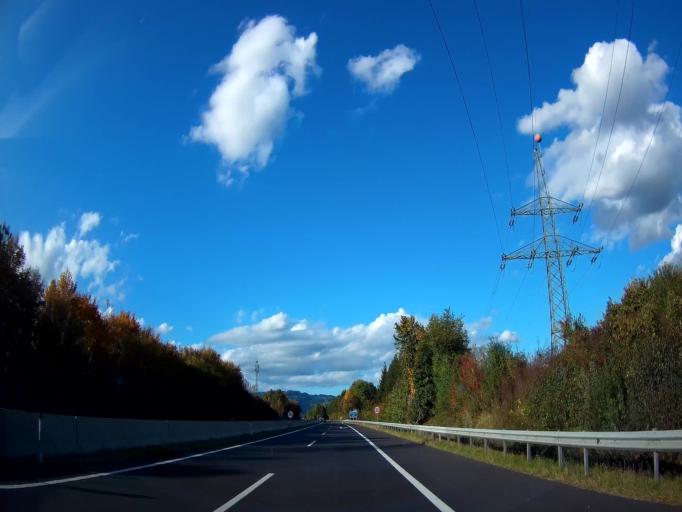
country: AT
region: Carinthia
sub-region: Politischer Bezirk Wolfsberg
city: Wolfsberg
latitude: 46.8170
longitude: 14.8226
